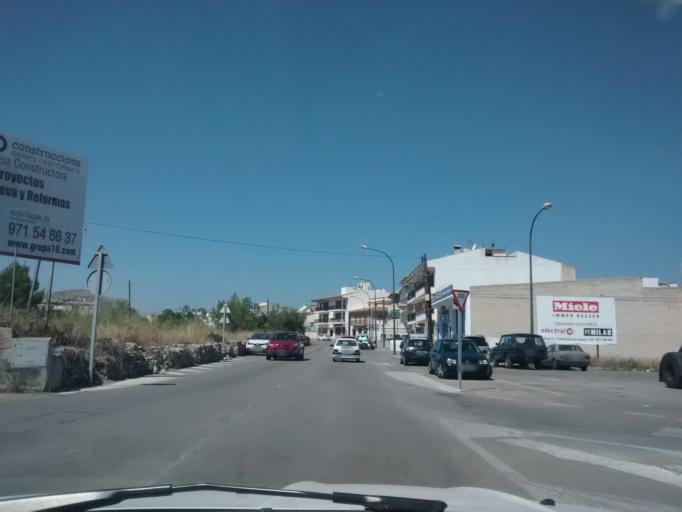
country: ES
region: Balearic Islands
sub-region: Illes Balears
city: Alcudia
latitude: 39.8529
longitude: 3.1282
